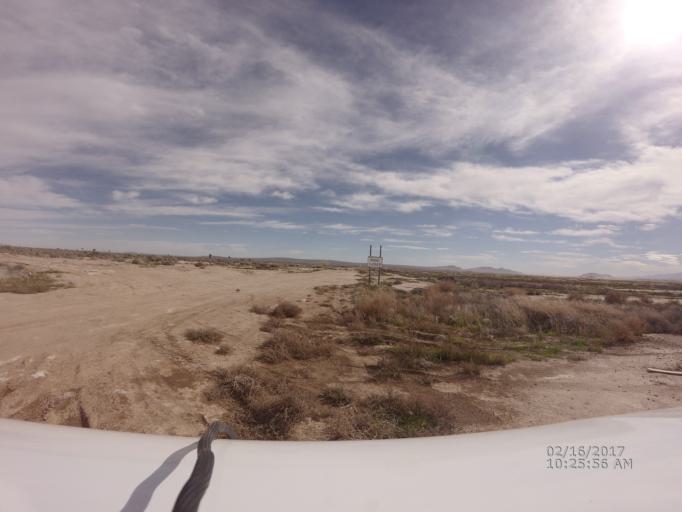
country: US
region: California
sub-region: Los Angeles County
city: Lake Los Angeles
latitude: 34.7342
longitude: -117.9521
